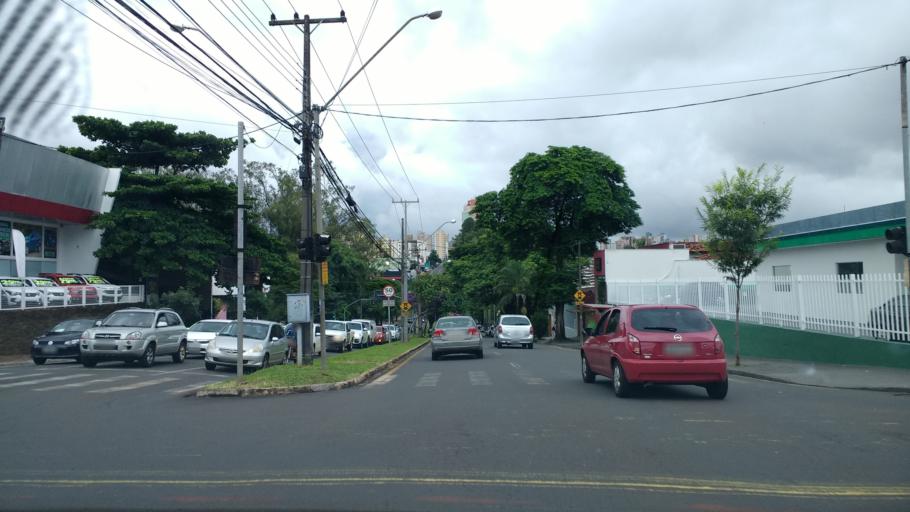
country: BR
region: Parana
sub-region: Londrina
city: Londrina
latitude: -23.3319
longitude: -51.1676
